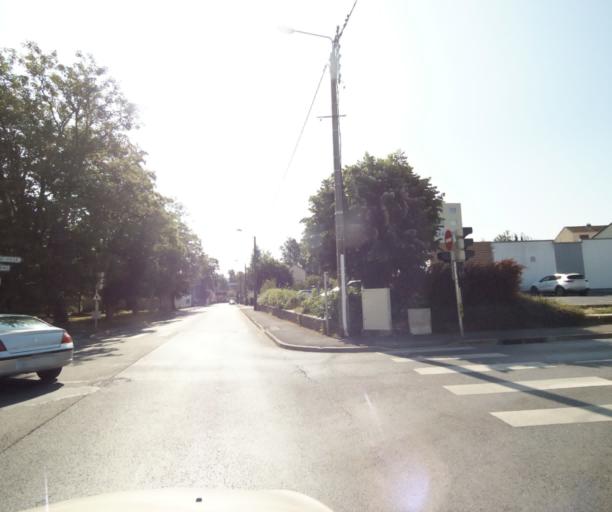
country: FR
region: Champagne-Ardenne
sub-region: Departement des Ardennes
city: Charleville-Mezieres
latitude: 49.7804
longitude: 4.7101
